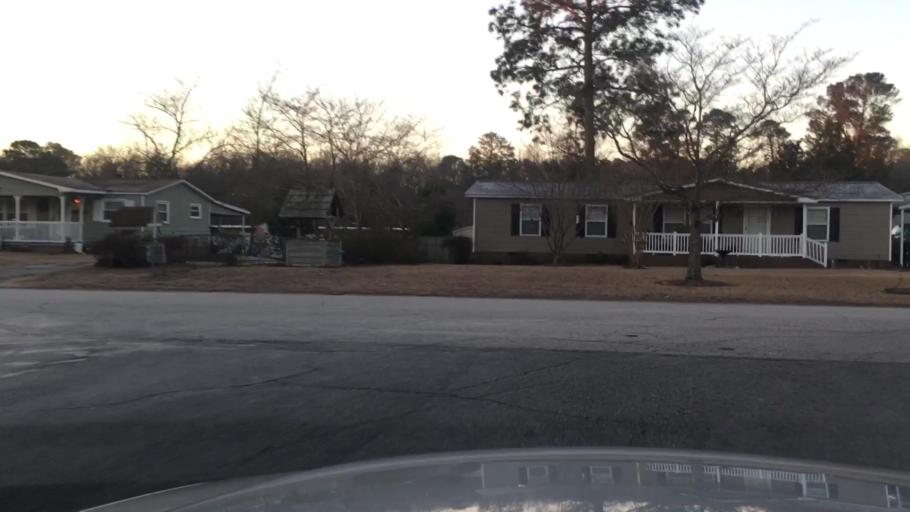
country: US
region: North Carolina
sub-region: Cumberland County
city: Hope Mills
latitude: 34.9906
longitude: -78.9006
